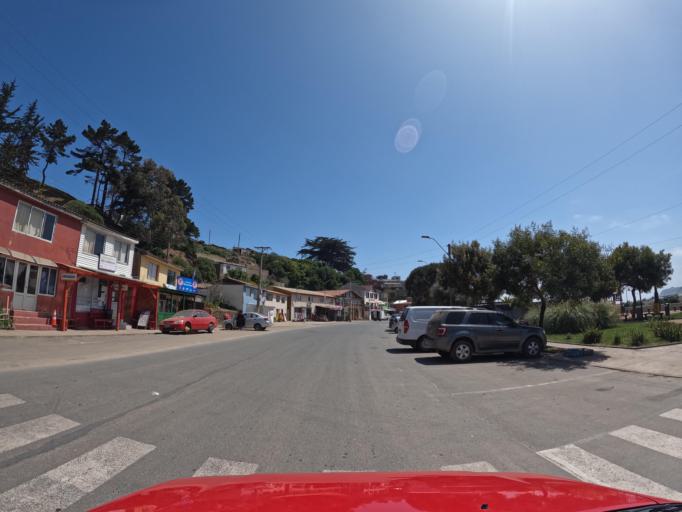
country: CL
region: O'Higgins
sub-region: Provincia de Colchagua
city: Santa Cruz
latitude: -34.6420
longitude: -72.0428
